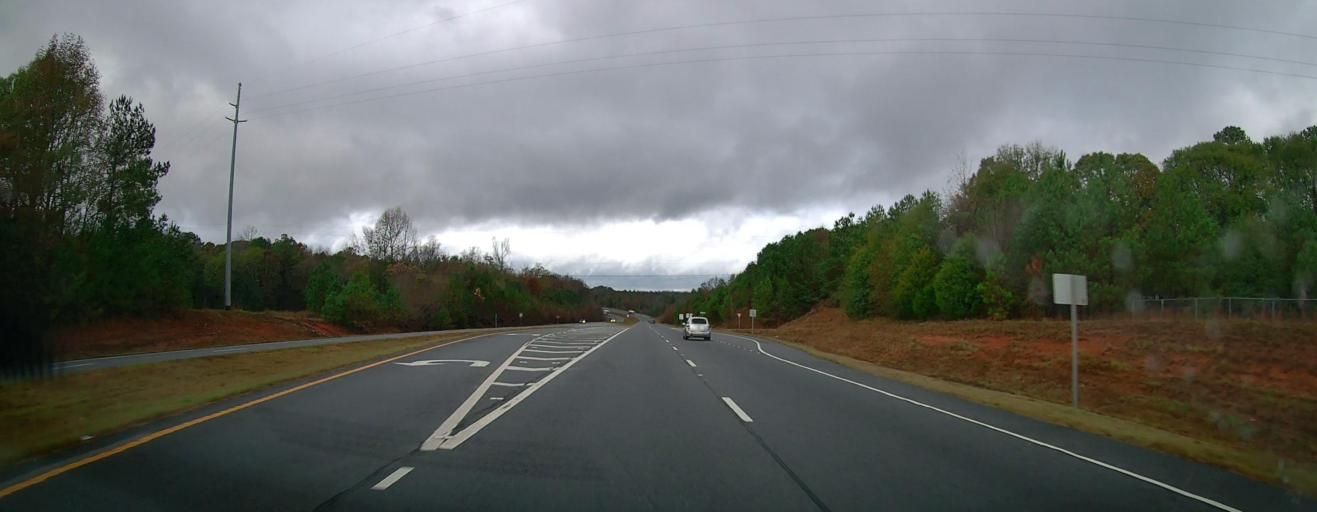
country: US
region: Georgia
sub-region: Clarke County
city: Country Club Estates
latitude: 34.0533
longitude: -83.4086
